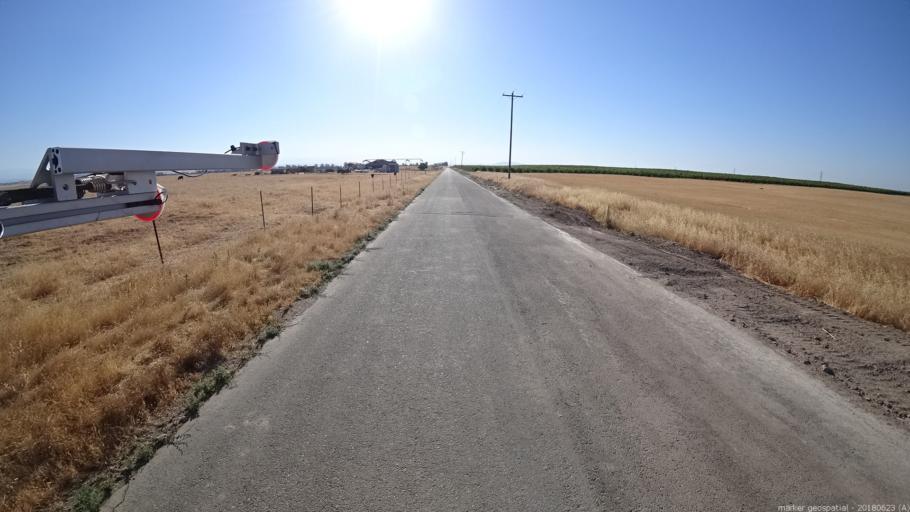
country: US
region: California
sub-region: Madera County
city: Bonadelle Ranchos-Madera Ranchos
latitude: 36.9520
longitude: -119.8176
